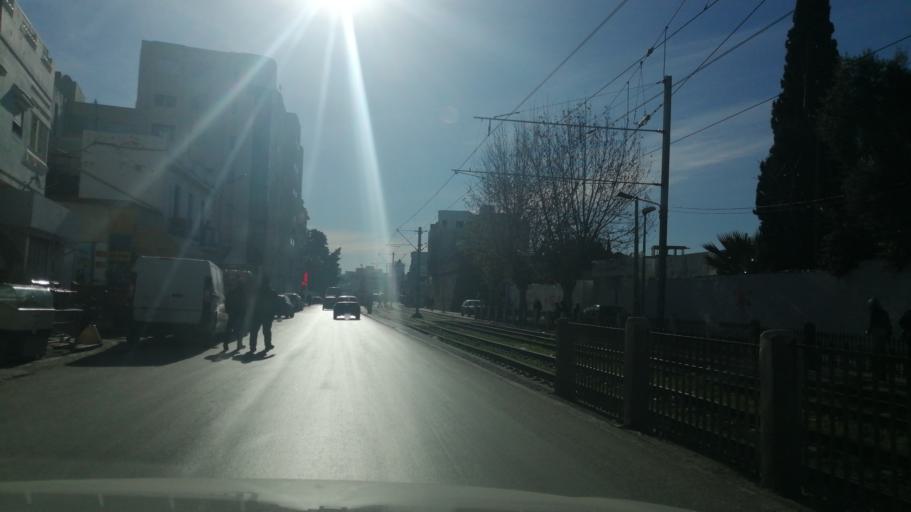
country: TN
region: Tunis
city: Tunis
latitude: 36.8116
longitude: 10.1710
